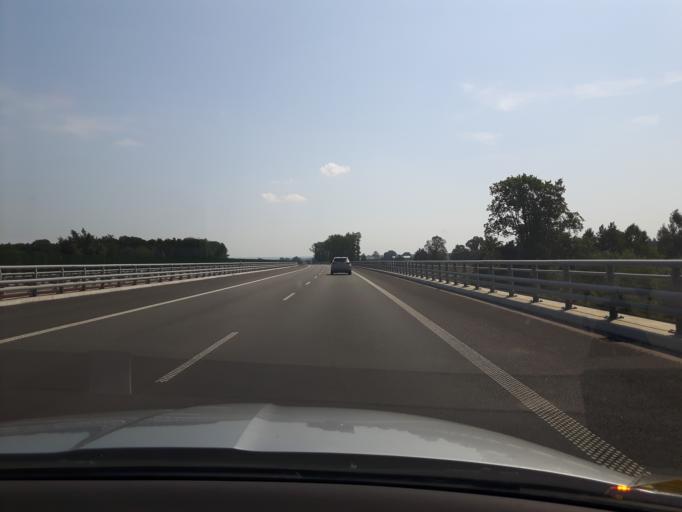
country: PL
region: Warmian-Masurian Voivodeship
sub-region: Powiat elblaski
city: Gronowo Elblaskie
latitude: 54.1655
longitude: 19.2418
